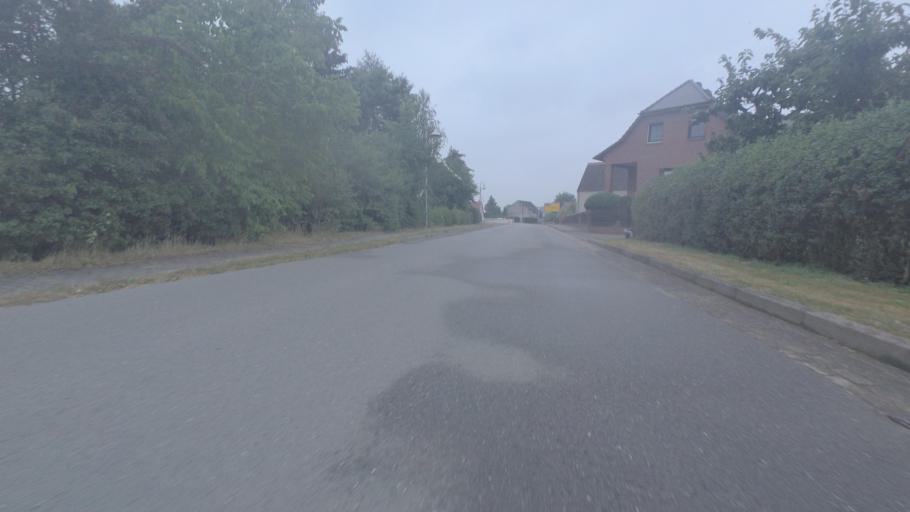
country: DE
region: Brandenburg
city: Heiligengrabe
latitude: 53.1182
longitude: 12.3765
